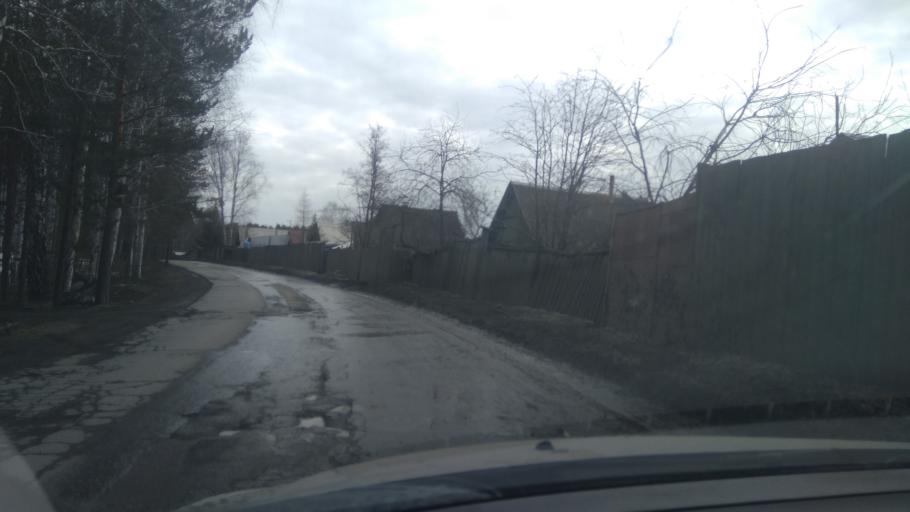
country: RU
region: Sverdlovsk
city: Severka
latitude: 56.8439
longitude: 60.3837
